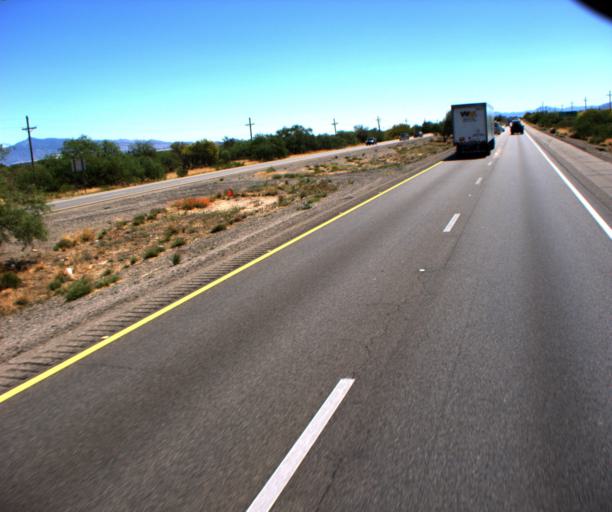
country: US
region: Arizona
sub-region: Pima County
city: Vail
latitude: 32.0893
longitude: -110.8180
